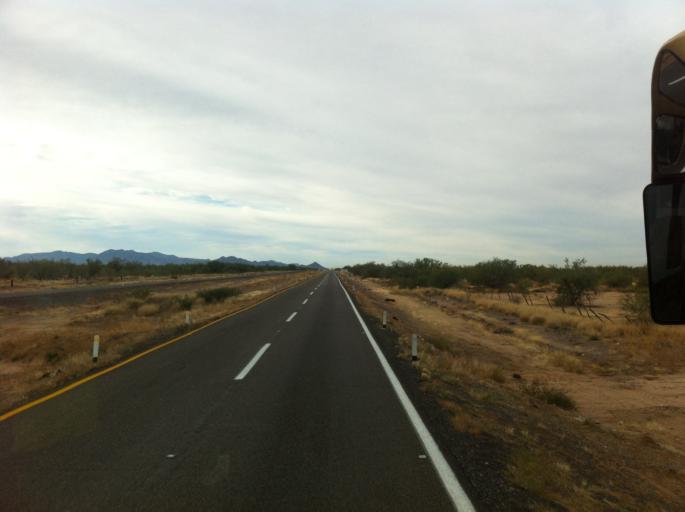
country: MX
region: Sonora
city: Hermosillo
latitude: 28.7750
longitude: -110.9662
